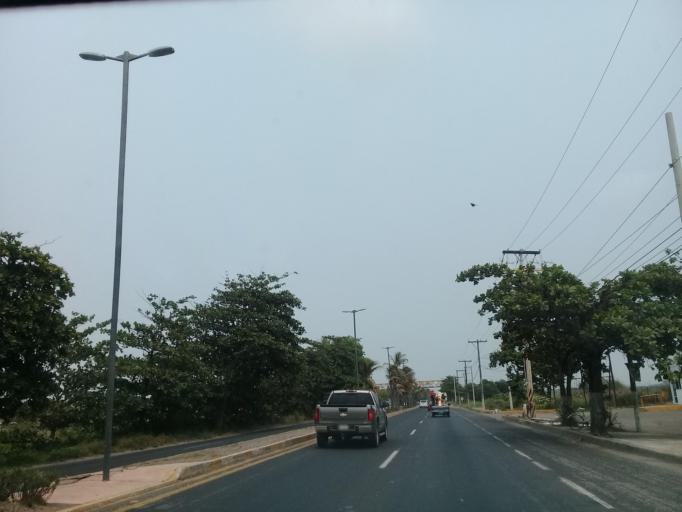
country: MX
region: Veracruz
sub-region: Veracruz
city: Hacienda Sotavento
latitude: 19.1480
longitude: -96.1694
